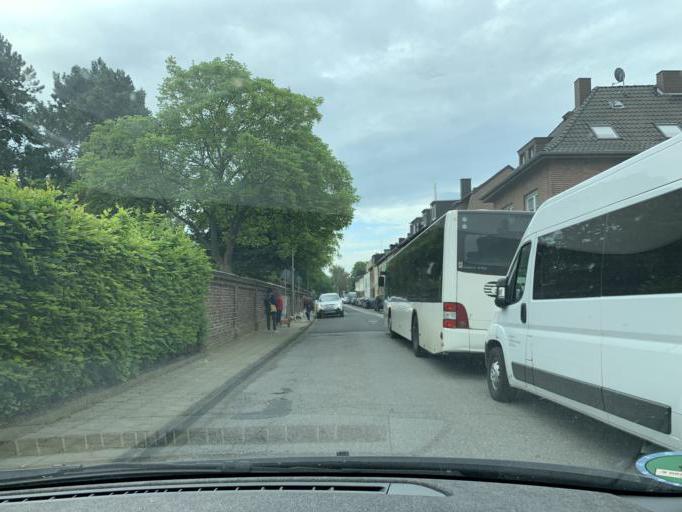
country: DE
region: North Rhine-Westphalia
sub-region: Regierungsbezirk Koln
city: Dueren
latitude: 50.8274
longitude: 6.4651
